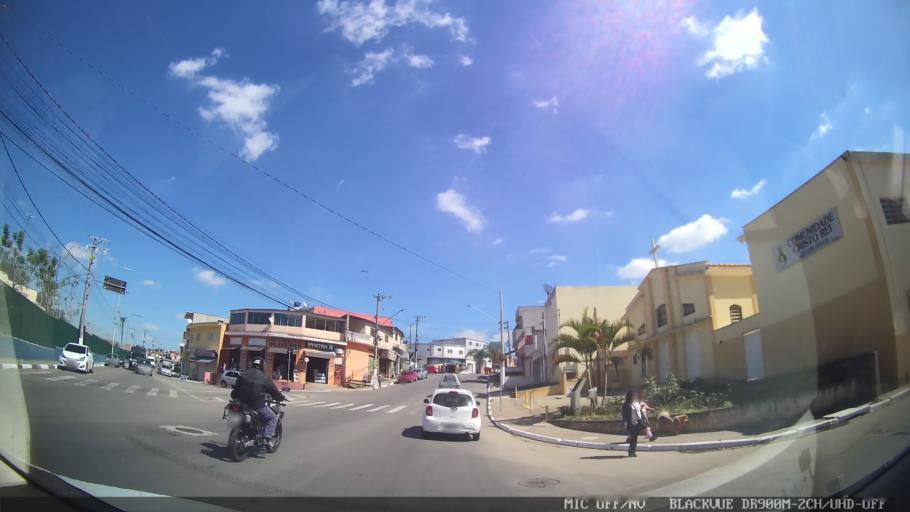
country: BR
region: Sao Paulo
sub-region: Cajamar
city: Cajamar
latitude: -23.4236
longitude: -46.8257
